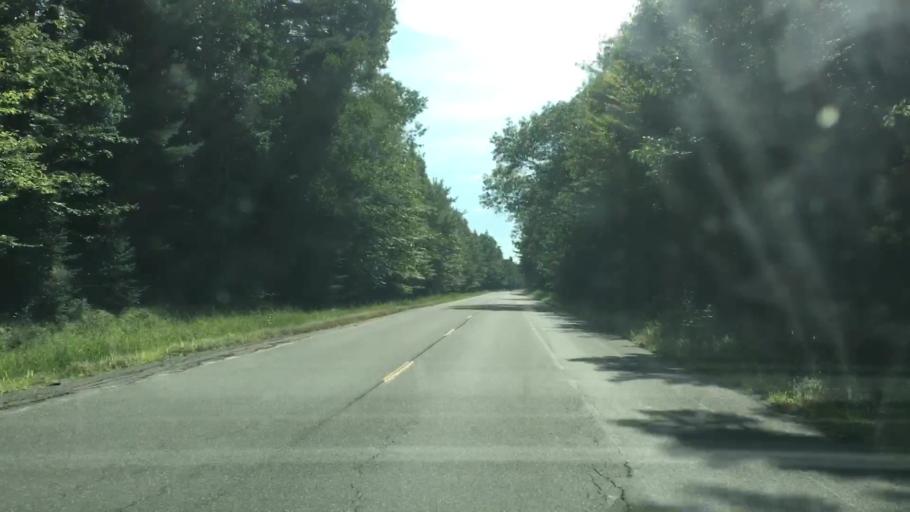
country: US
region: Maine
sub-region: Penobscot County
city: Lincoln
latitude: 45.3850
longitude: -68.5407
